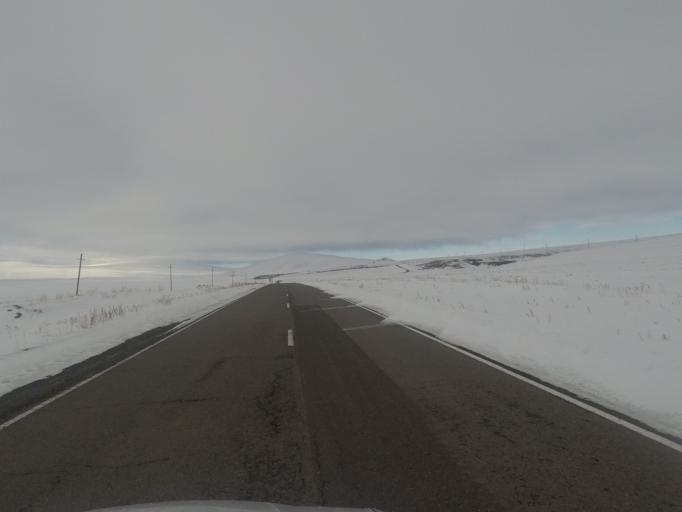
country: GE
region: Samtskhe-Javakheti
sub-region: Ninotsminda
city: Ninotsminda
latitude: 41.4271
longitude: 43.8361
